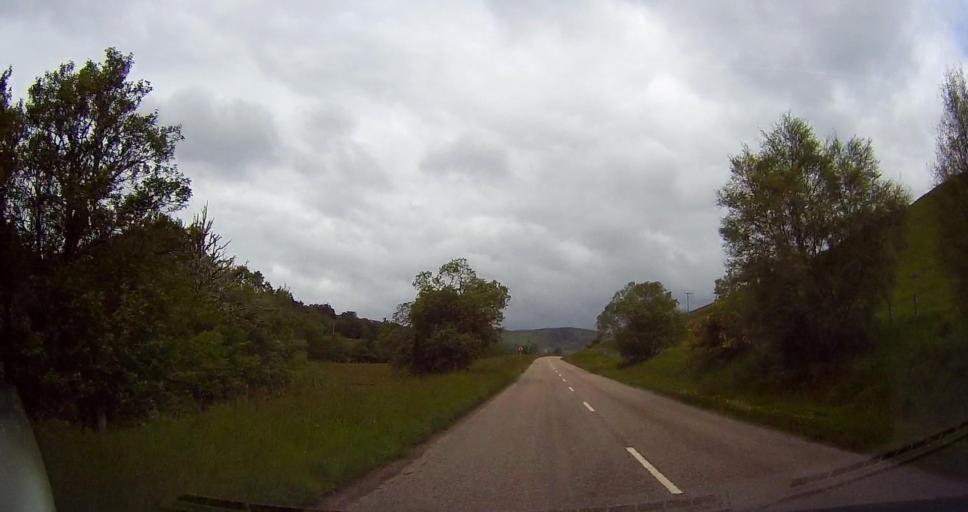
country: GB
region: Scotland
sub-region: Highland
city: Dornoch
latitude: 58.0050
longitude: -4.2272
